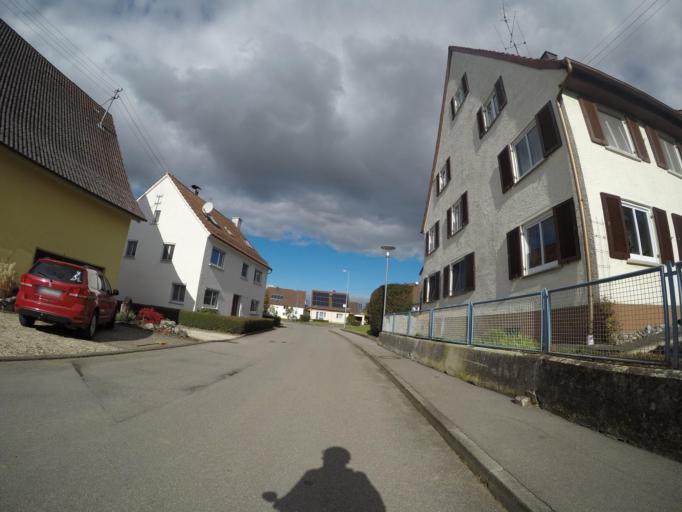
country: DE
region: Baden-Wuerttemberg
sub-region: Tuebingen Region
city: Oggelshausen
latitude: 48.0733
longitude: 9.6463
